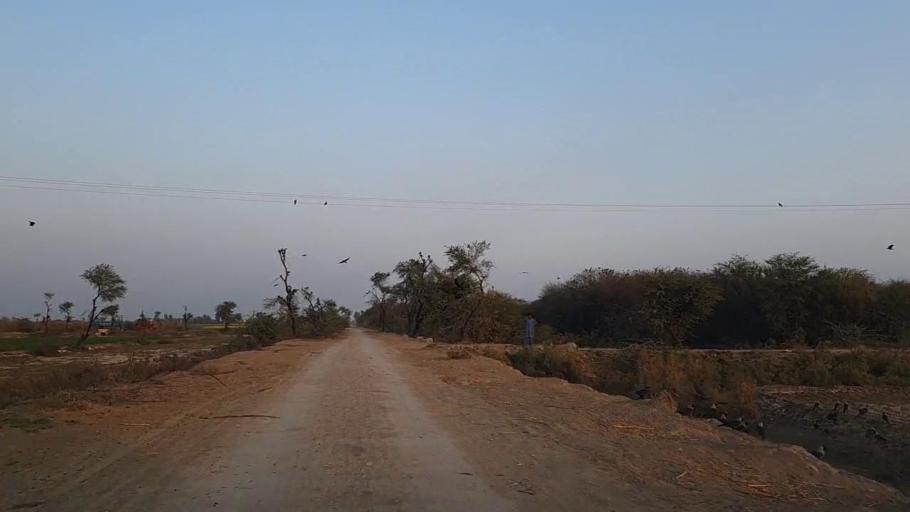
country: PK
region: Sindh
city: Jam Sahib
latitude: 26.3048
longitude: 68.5765
